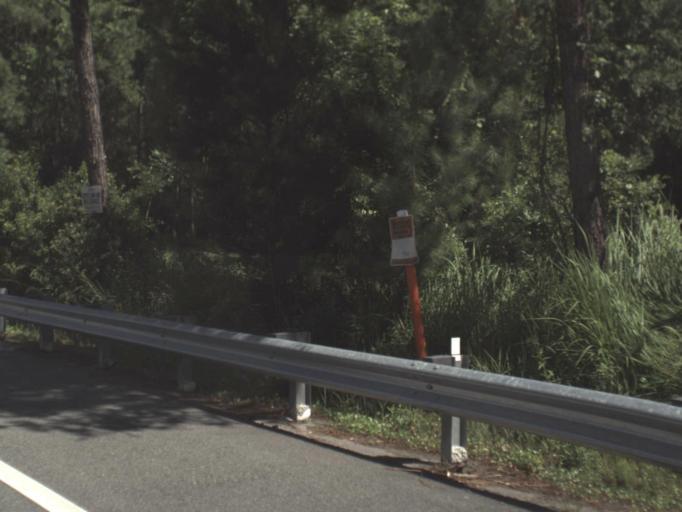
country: US
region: Florida
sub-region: Putnam County
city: Palatka
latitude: 29.6752
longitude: -81.7138
